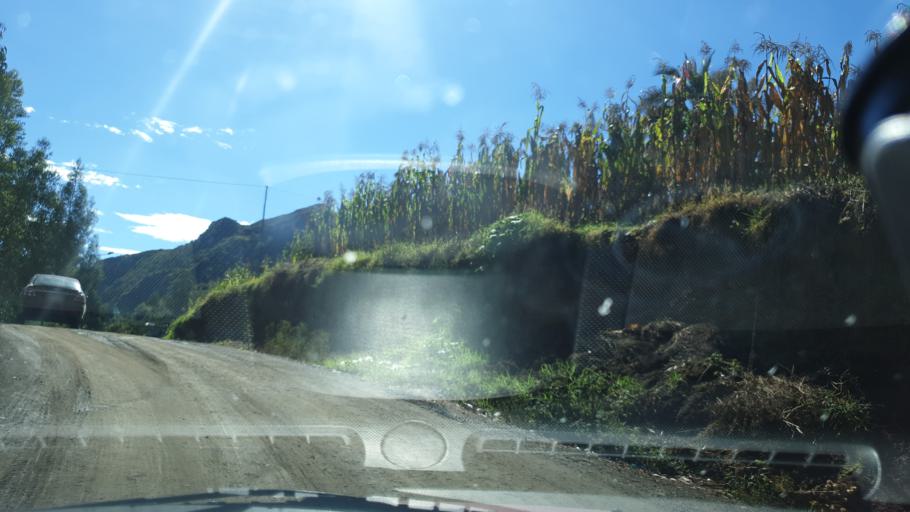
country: EC
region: Azuay
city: Llacao
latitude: -2.8760
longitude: -78.9071
